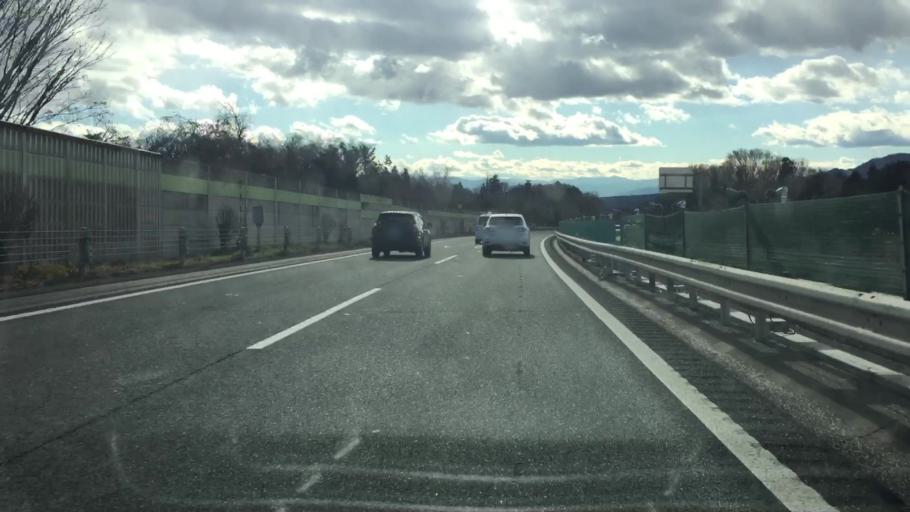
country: JP
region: Gunma
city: Shibukawa
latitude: 36.5319
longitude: 139.0461
